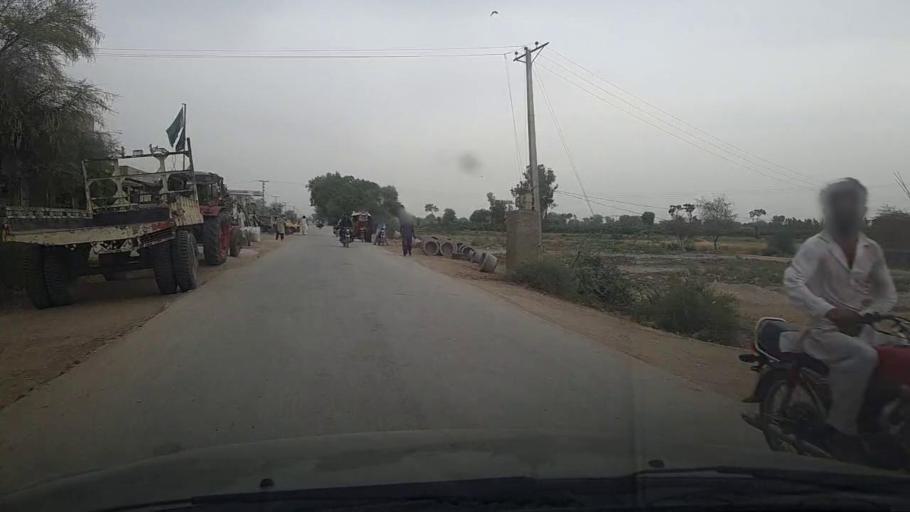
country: PK
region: Sindh
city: Daulatpur
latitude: 26.3137
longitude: 68.1013
